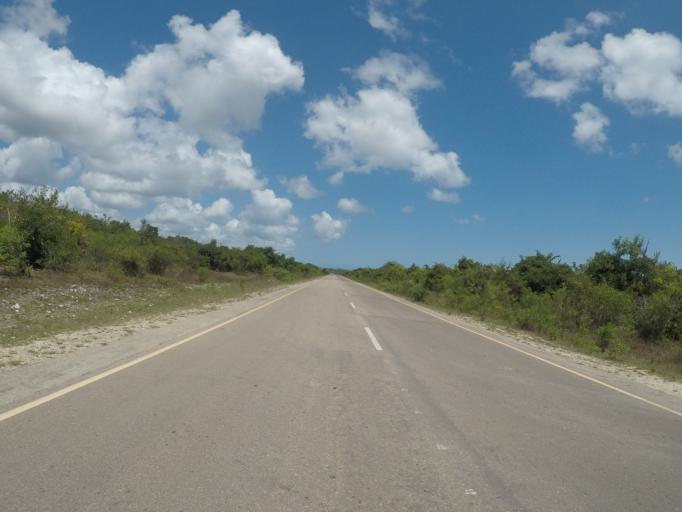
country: TZ
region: Zanzibar Central/South
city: Koani
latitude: -6.2716
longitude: 39.3632
